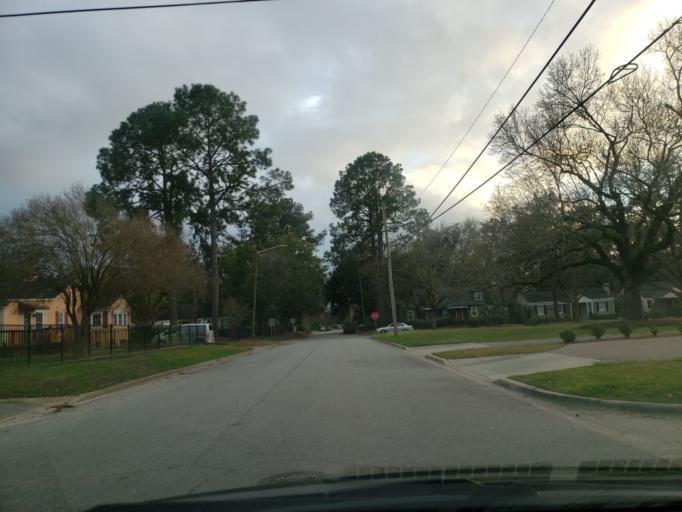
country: US
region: Georgia
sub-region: Chatham County
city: Thunderbolt
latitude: 32.0339
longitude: -81.0973
